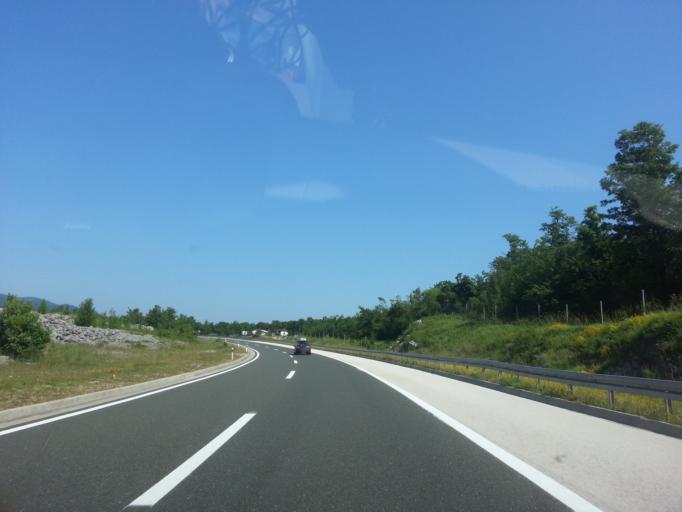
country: HR
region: Primorsko-Goranska
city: Matulji
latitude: 45.4250
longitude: 14.2987
